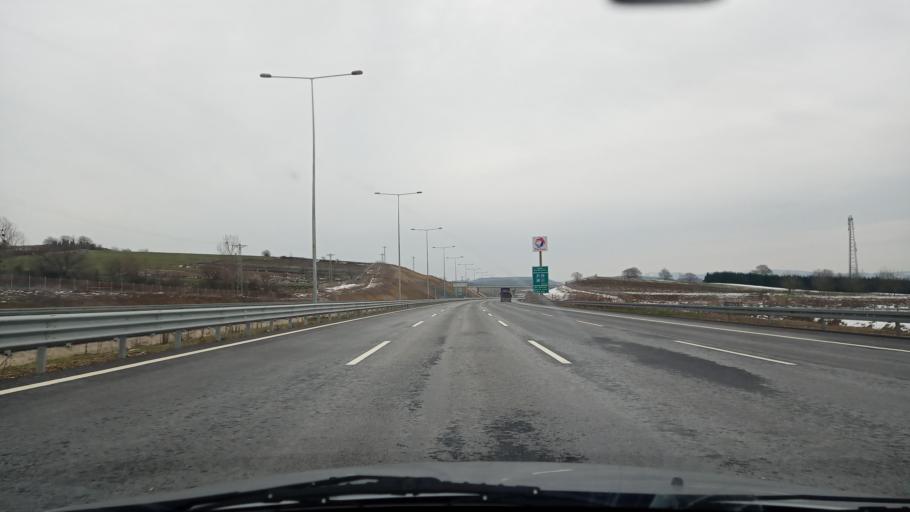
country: TR
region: Kocaeli
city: Derbent
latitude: 40.7967
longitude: 30.0642
